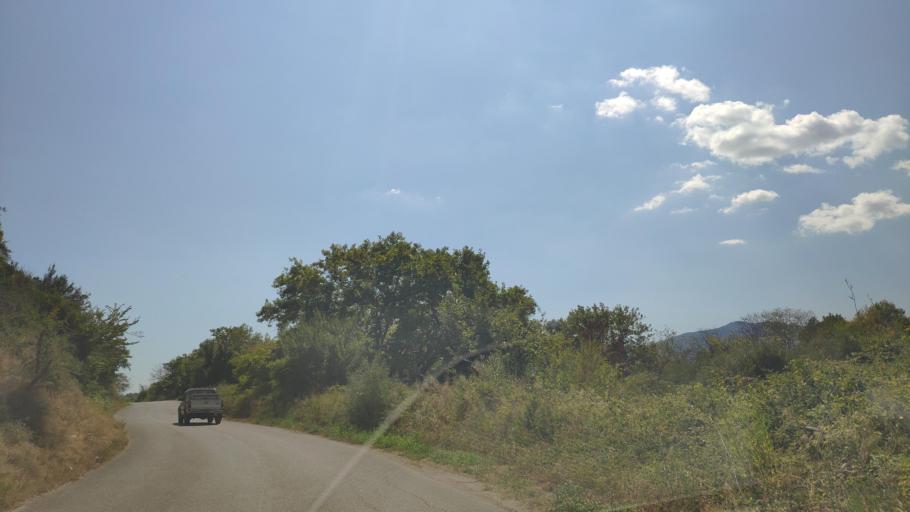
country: GR
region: Epirus
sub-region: Nomos Prevezis
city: Kanalaki
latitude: 39.3243
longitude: 20.6105
